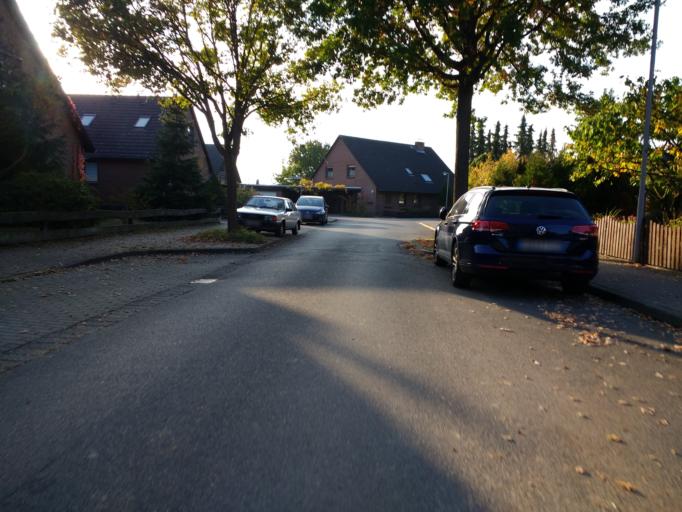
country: DE
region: Lower Saxony
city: Gifhorn
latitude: 52.4644
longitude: 10.5487
